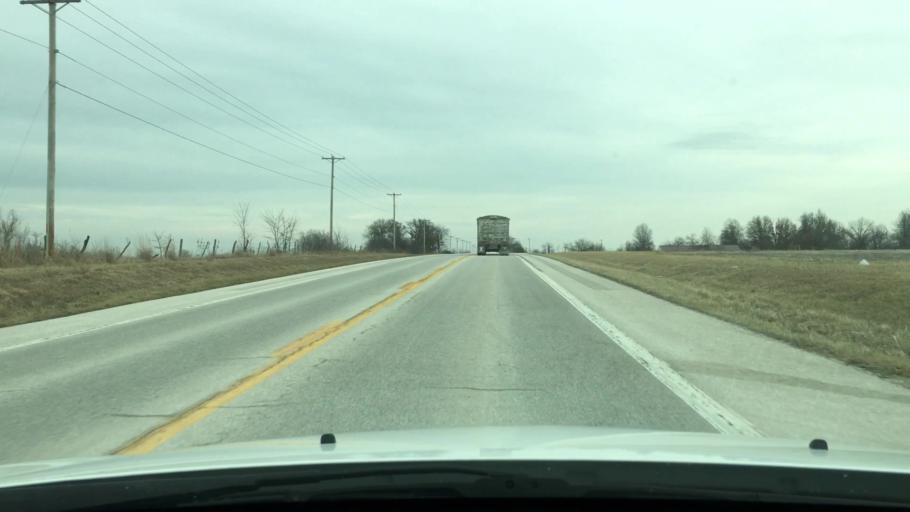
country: US
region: Missouri
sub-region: Pike County
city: Bowling Green
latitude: 39.3443
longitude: -91.2701
